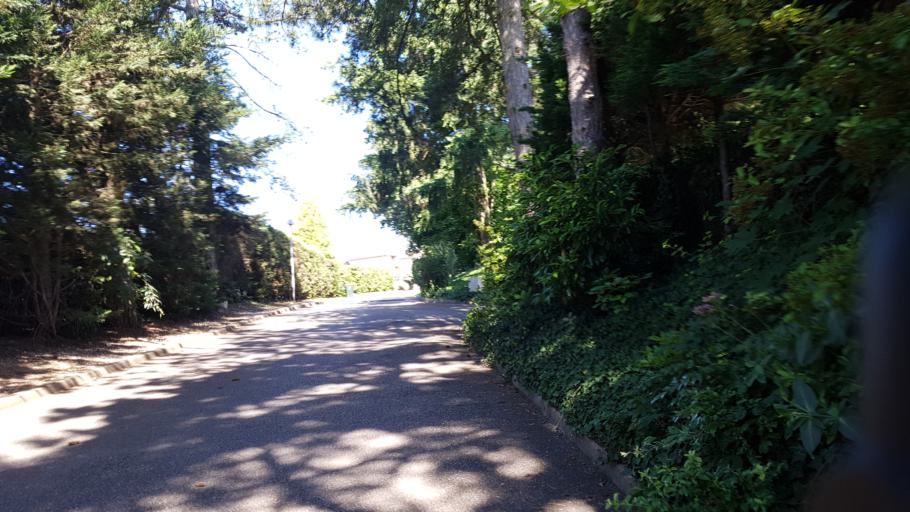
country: FR
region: Rhone-Alpes
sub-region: Departement du Rhone
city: Caluire-et-Cuire
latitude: 45.7995
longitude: 4.8554
